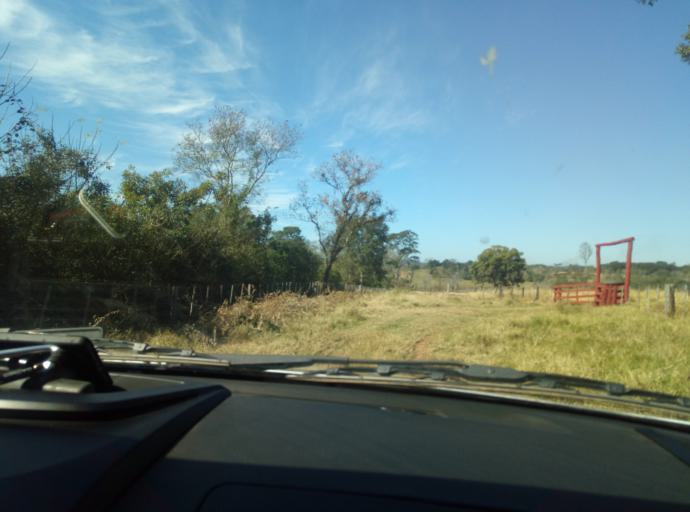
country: PY
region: Caaguazu
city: Carayao
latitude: -25.1766
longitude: -56.3012
